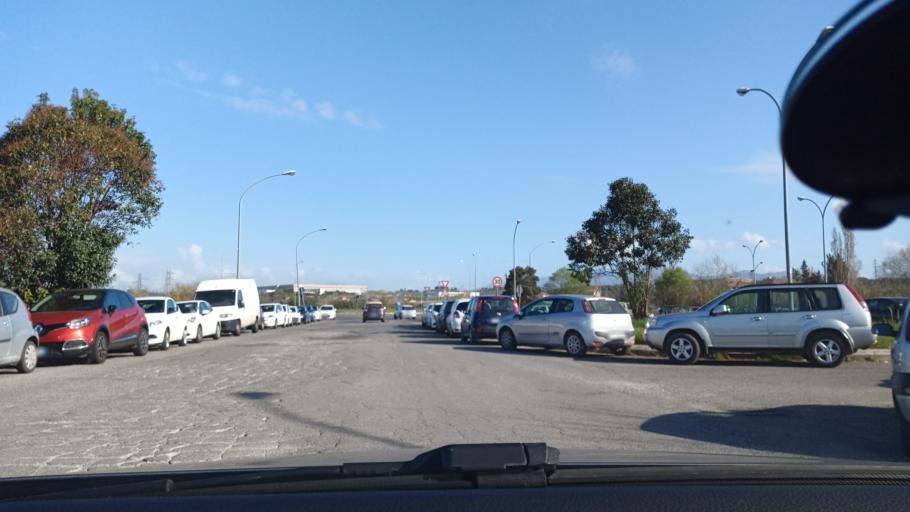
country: IT
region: Latium
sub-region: Citta metropolitana di Roma Capitale
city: Fiano Romano
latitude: 42.1557
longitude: 12.6454
